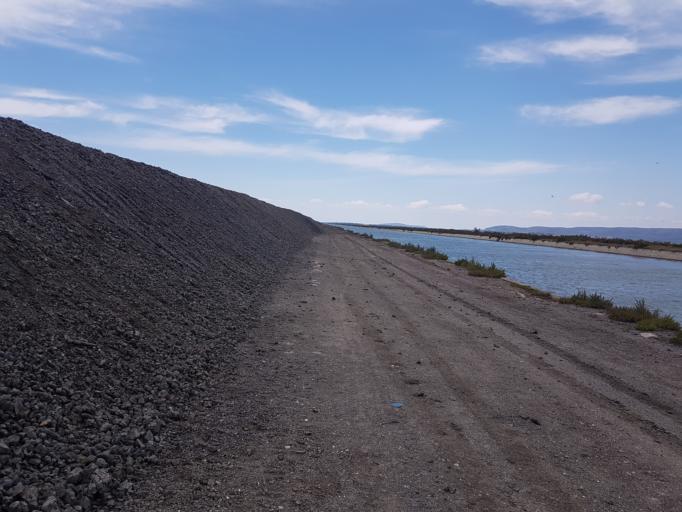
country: FR
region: Languedoc-Roussillon
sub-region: Departement de l'Herault
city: Villeneuve-les-Maguelone
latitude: 43.5080
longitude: 3.8687
